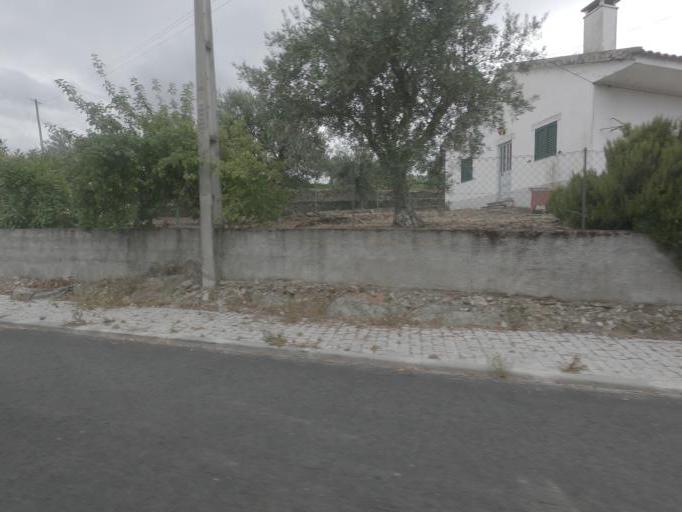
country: PT
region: Vila Real
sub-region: Sabrosa
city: Sabrosa
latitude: 41.2124
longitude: -7.5254
